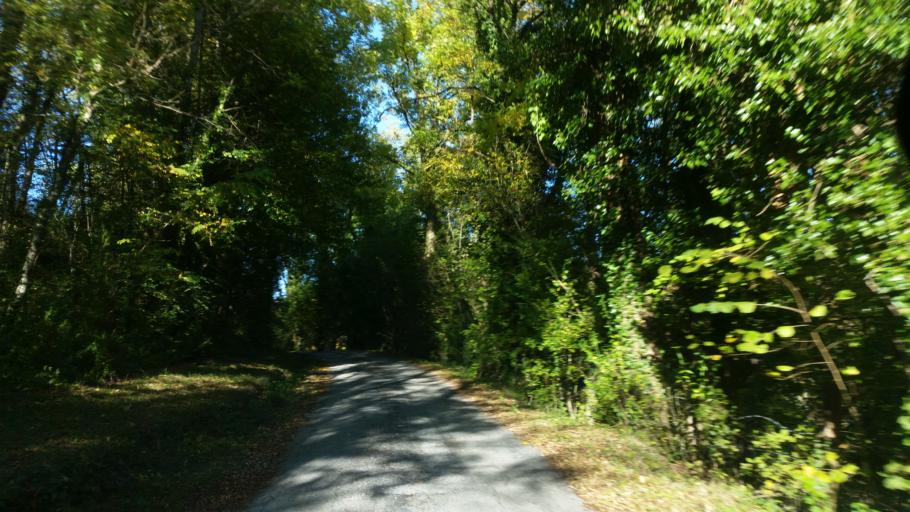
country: FR
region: Franche-Comte
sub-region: Departement du Doubs
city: Levier
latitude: 47.0086
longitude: 6.0381
